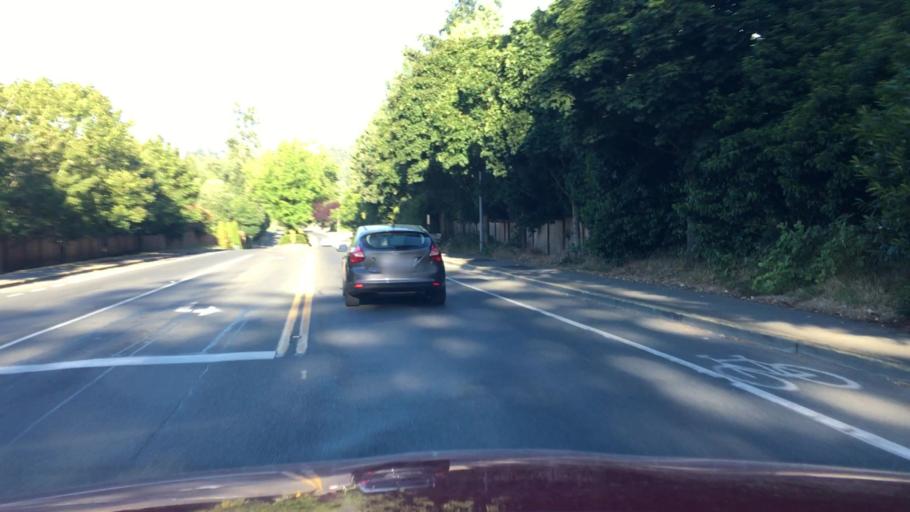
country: CA
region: British Columbia
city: Victoria
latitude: 48.5038
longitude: -123.3545
